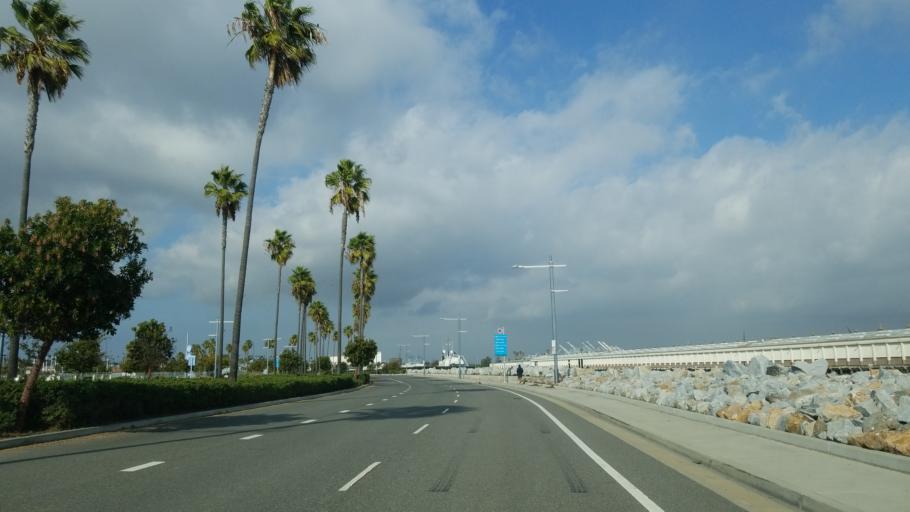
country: US
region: California
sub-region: Los Angeles County
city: San Pedro
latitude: 33.7188
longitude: -118.2742
